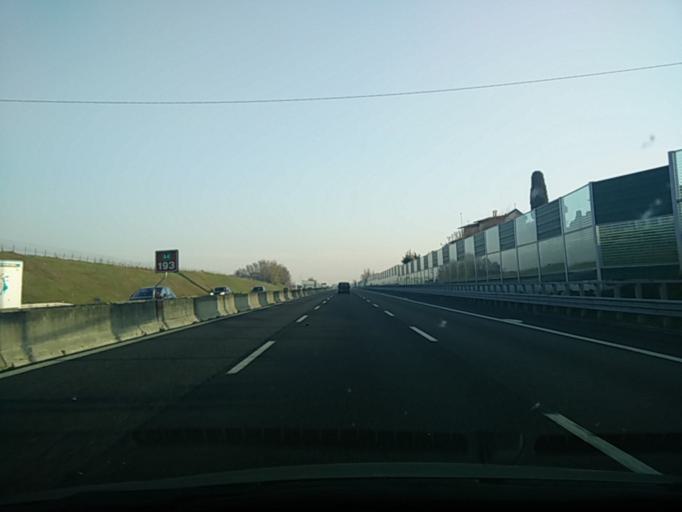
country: IT
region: Lombardy
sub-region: Provincia di Brescia
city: Adro
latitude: 45.6038
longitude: 9.9480
